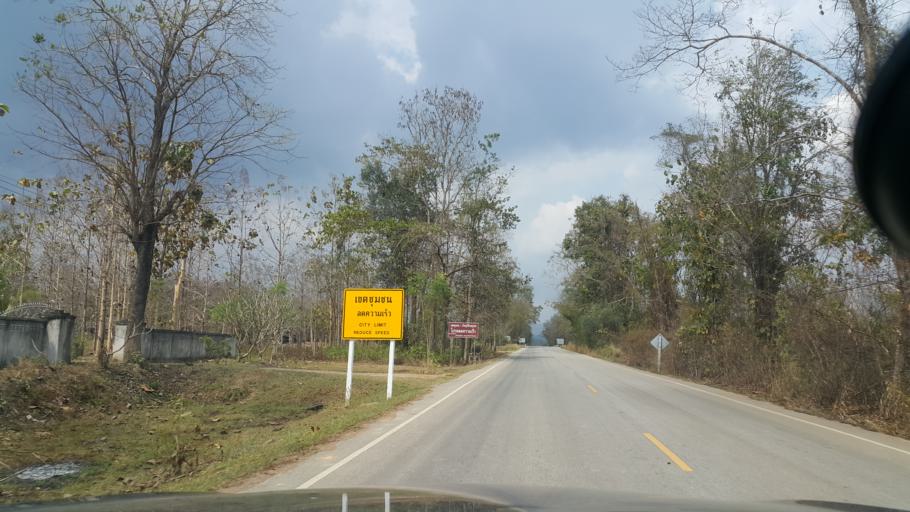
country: TH
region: Lampang
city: Thoen
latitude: 17.4681
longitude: 99.3595
